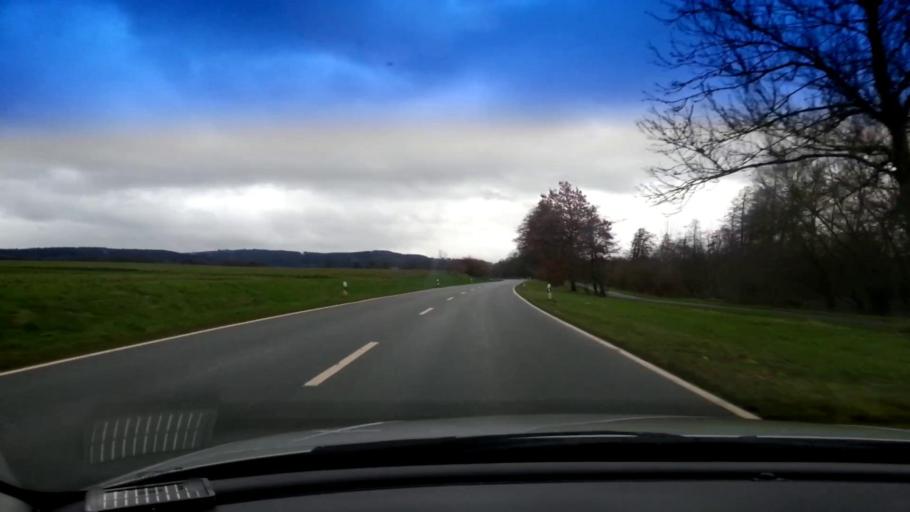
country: DE
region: Bavaria
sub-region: Upper Franconia
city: Ebensfeld
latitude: 50.0458
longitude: 10.9939
